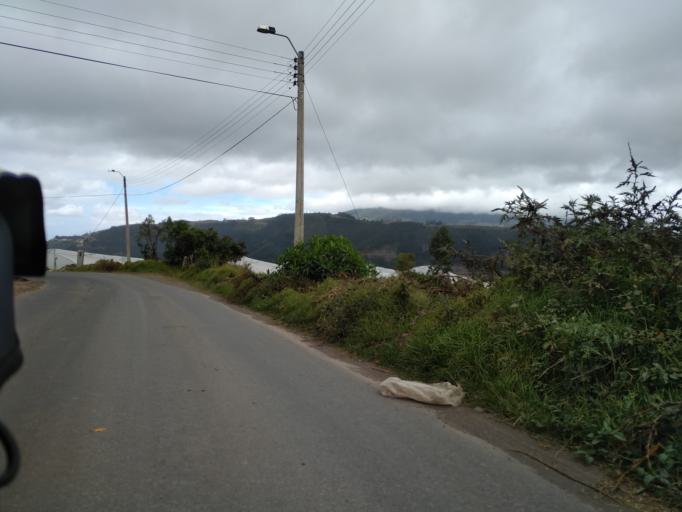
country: EC
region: Carchi
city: El Angel
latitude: 0.6271
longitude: -77.9347
